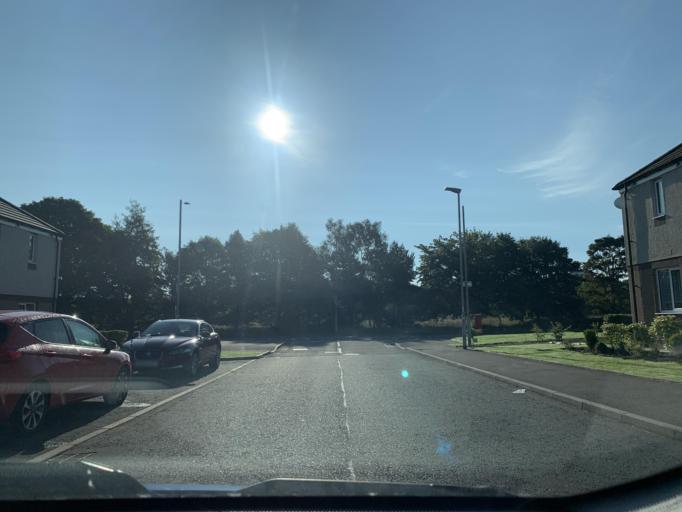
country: GB
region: Scotland
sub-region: East Renfrewshire
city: Giffnock
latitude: 55.8197
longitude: -4.3318
